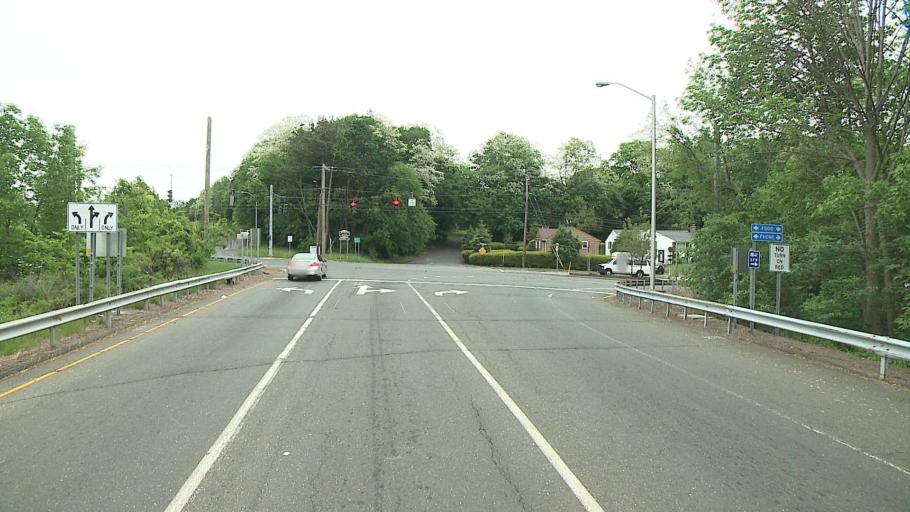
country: US
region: Connecticut
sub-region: Hartford County
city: West Hartford
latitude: 41.7348
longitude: -72.7436
